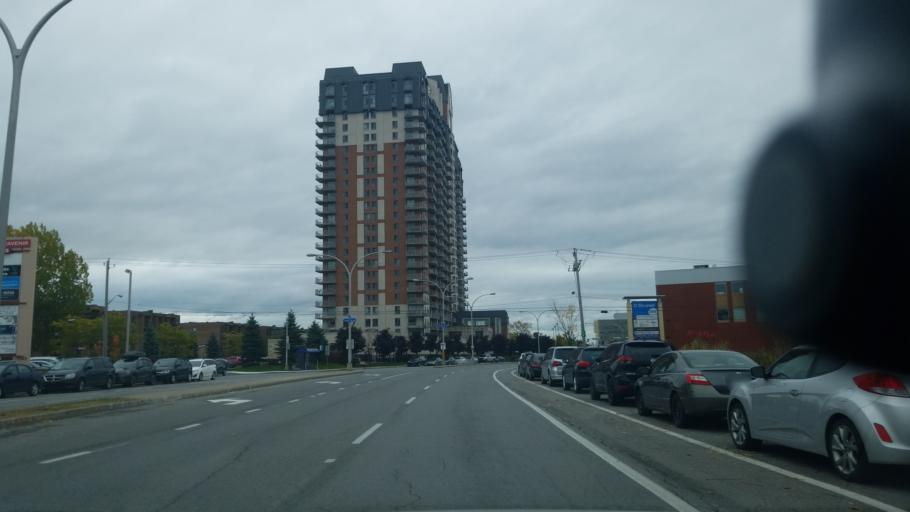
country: CA
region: Quebec
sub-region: Laval
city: Laval
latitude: 45.5646
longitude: -73.7250
